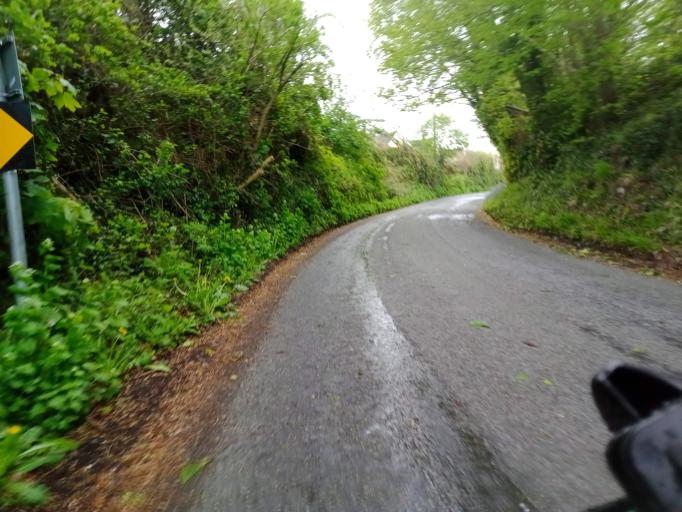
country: IE
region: Leinster
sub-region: Kilkenny
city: Kilkenny
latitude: 52.6745
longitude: -7.2581
